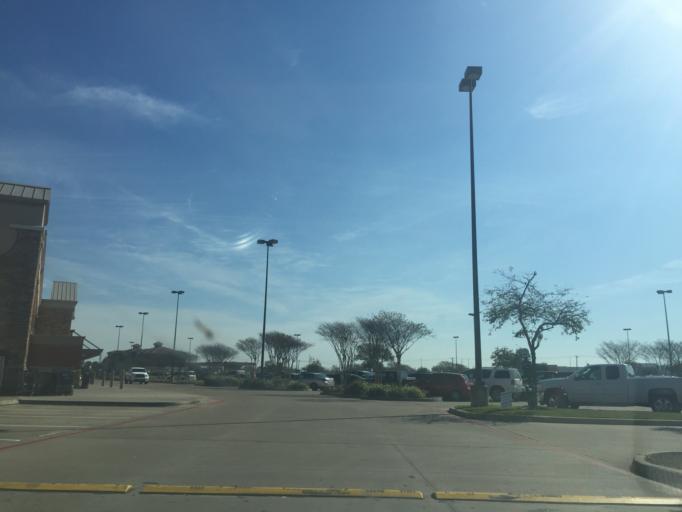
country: US
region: Texas
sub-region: Galveston County
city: Clear Lake Shores
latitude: 29.5072
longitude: -95.0420
